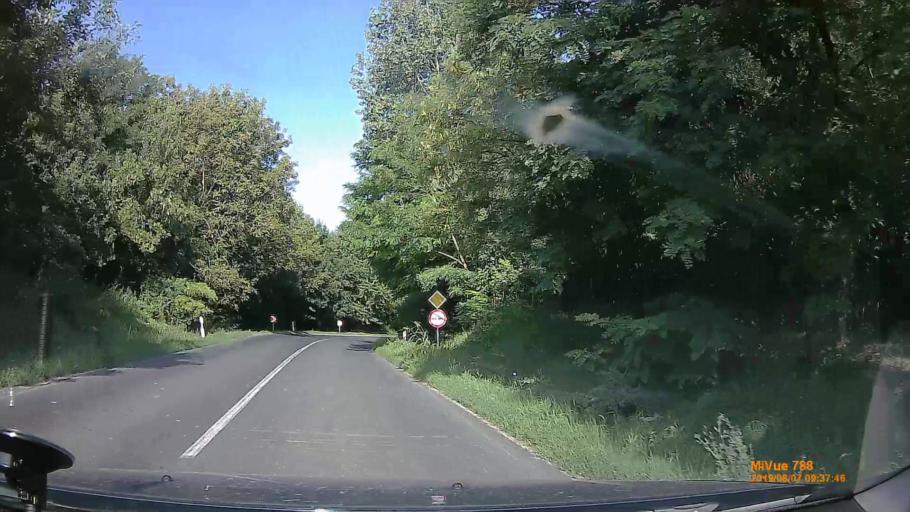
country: HU
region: Zala
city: Sarmellek
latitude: 46.7226
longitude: 17.0967
